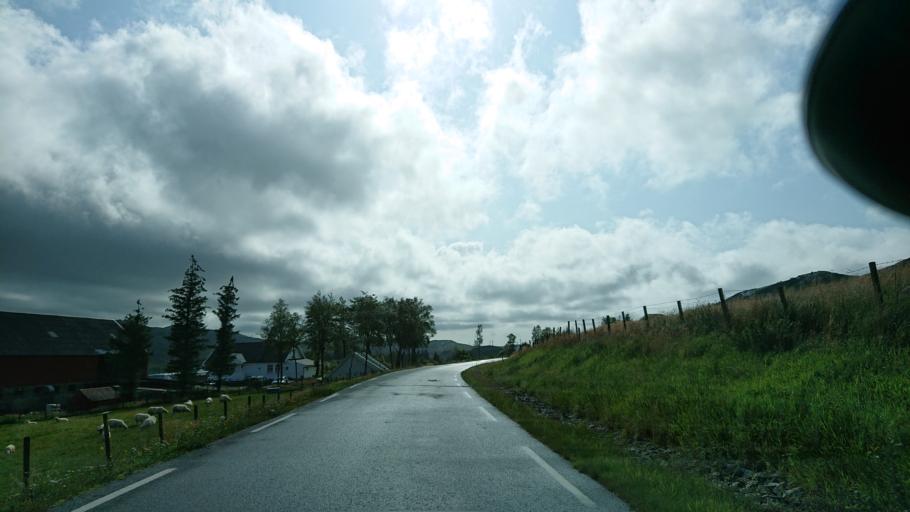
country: NO
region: Rogaland
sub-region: Gjesdal
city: Algard
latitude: 58.6864
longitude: 5.8713
